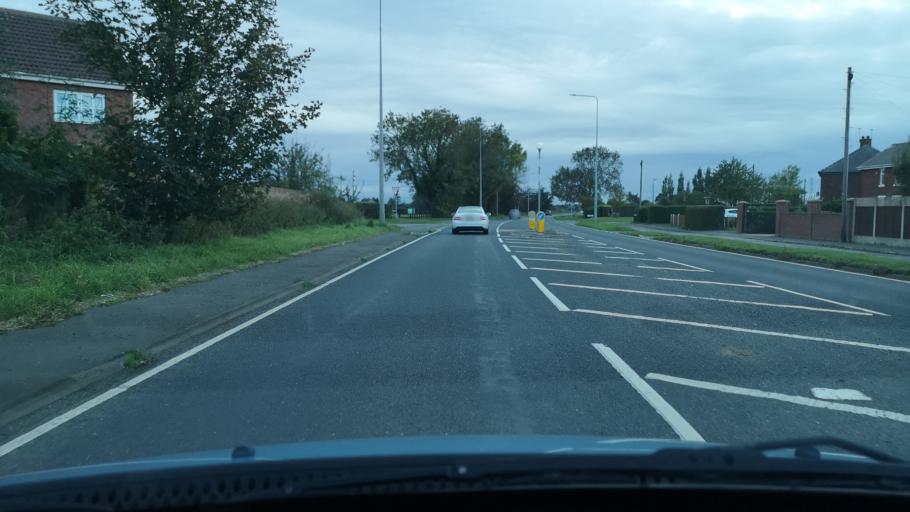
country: GB
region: England
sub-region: North Lincolnshire
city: Gunness
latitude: 53.5784
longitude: -0.7433
